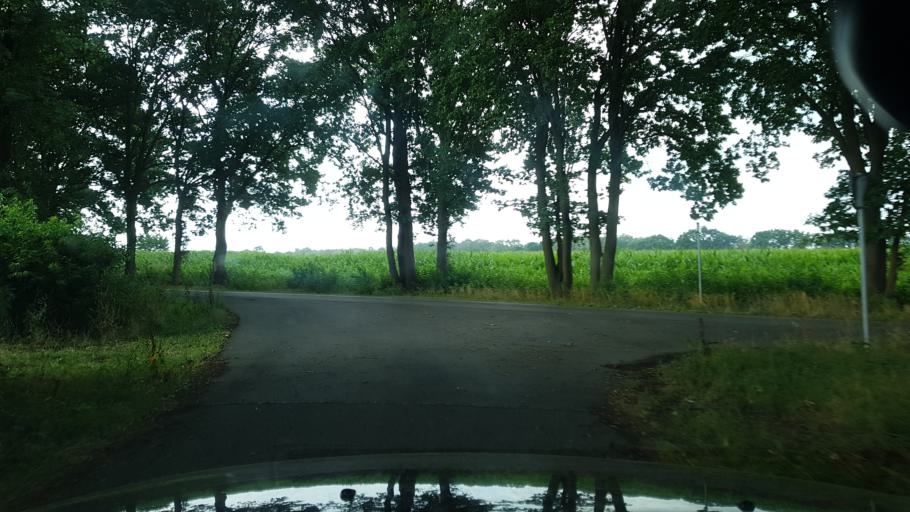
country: DE
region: Lower Saxony
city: Wehrbleck
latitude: 52.6764
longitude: 8.7196
